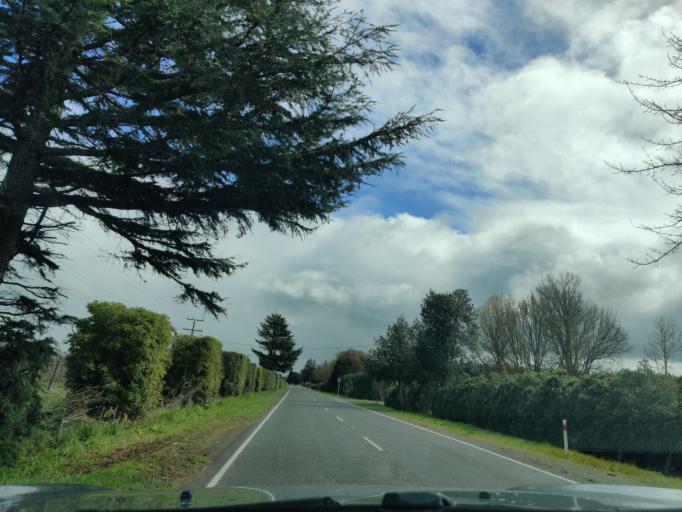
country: NZ
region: Hawke's Bay
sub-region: Hastings District
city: Hastings
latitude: -39.6783
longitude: 176.8554
